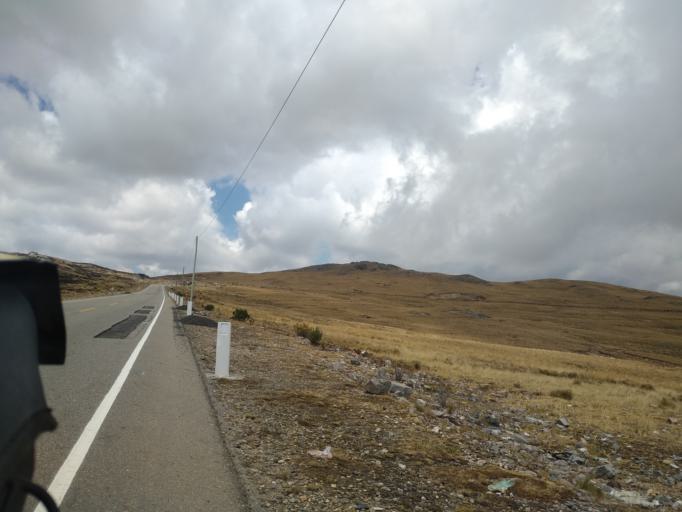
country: PE
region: La Libertad
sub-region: Provincia de Santiago de Chuco
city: Quiruvilca
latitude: -7.9460
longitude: -78.1903
